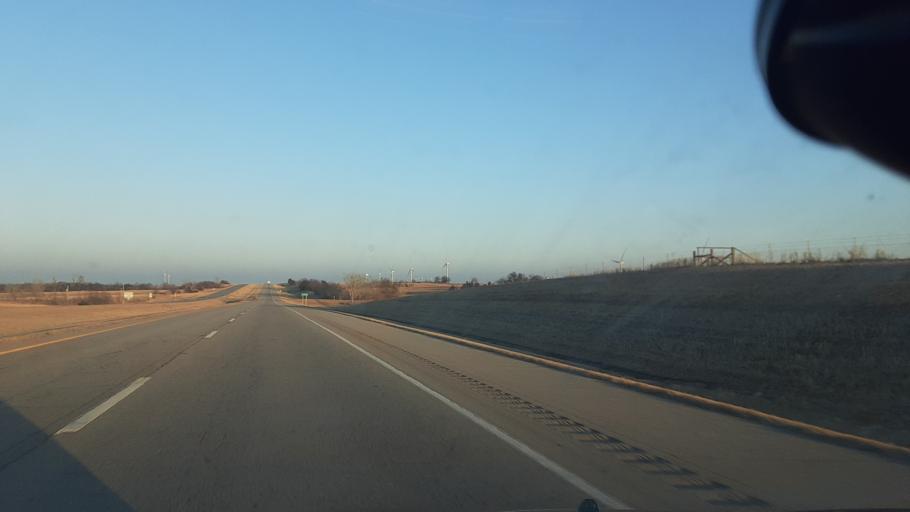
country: US
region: Oklahoma
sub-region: Noble County
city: Perry
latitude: 36.3977
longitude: -97.4482
